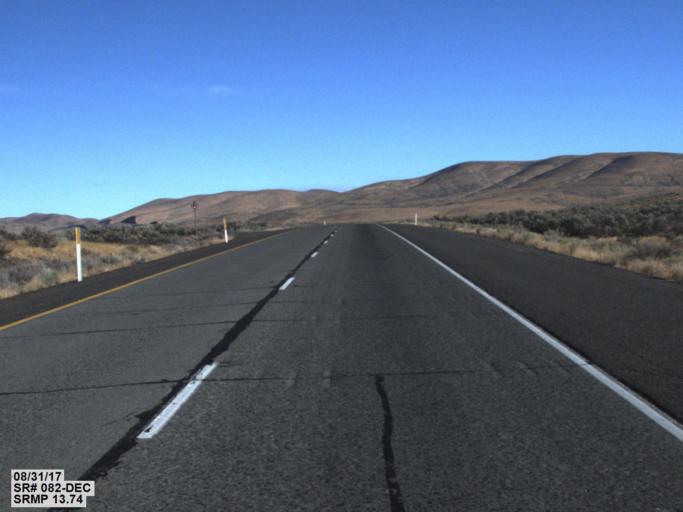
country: US
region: Washington
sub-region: Kittitas County
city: Kittitas
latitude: 46.8178
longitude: -120.3556
